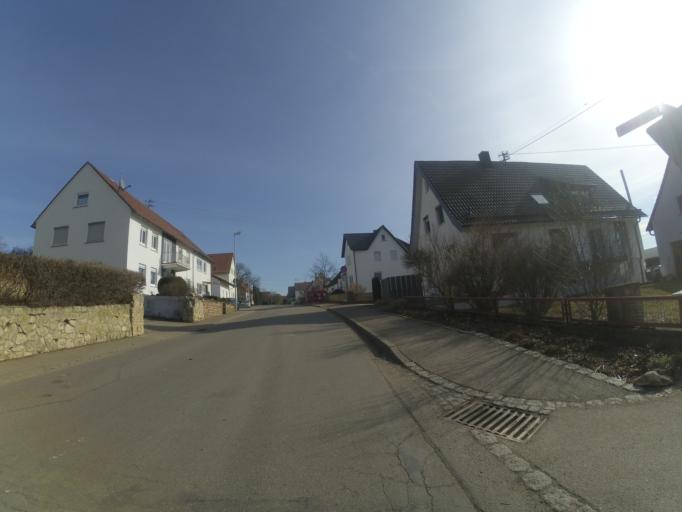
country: DE
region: Baden-Wuerttemberg
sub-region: Tuebingen Region
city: Bernstadt
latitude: 48.4852
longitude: 10.0309
